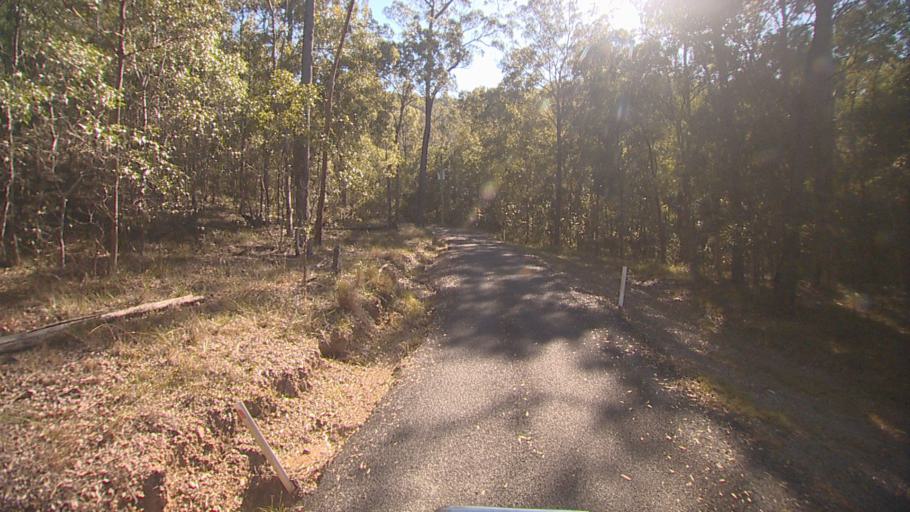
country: AU
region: Queensland
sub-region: Logan
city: Windaroo
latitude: -27.7884
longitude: 153.1716
